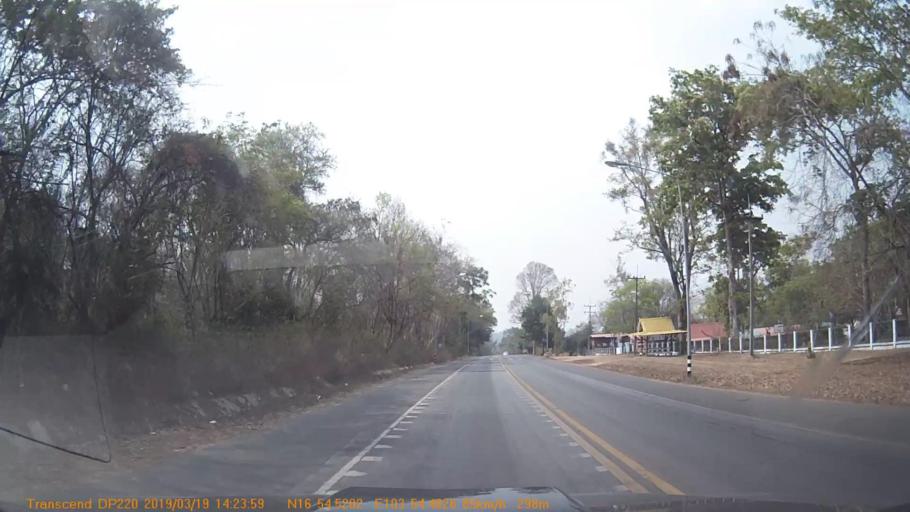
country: TH
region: Sakon Nakhon
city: Phu Phan
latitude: 16.9092
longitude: 103.9076
